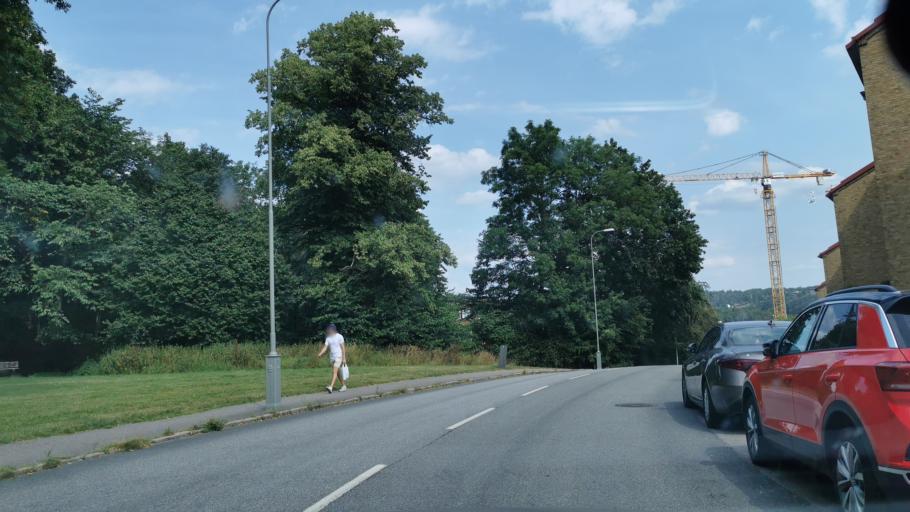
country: SE
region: Vaestra Goetaland
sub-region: Molndal
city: Moelndal
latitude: 57.6814
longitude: 11.9959
